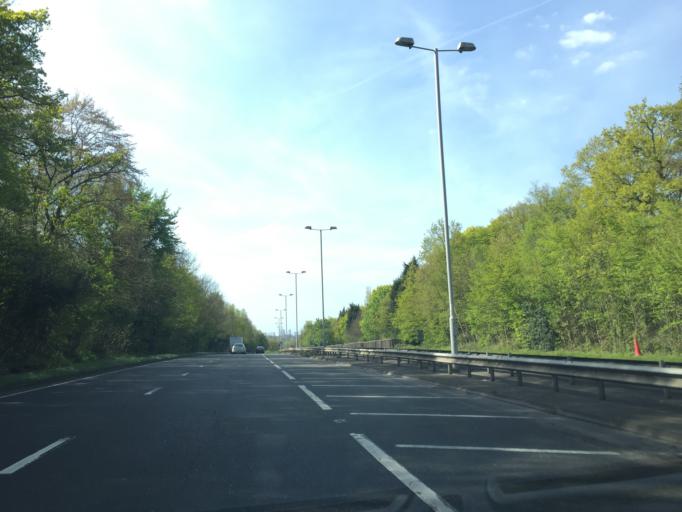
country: GB
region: England
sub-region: Greater London
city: Sidcup
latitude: 51.4219
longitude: 0.0925
